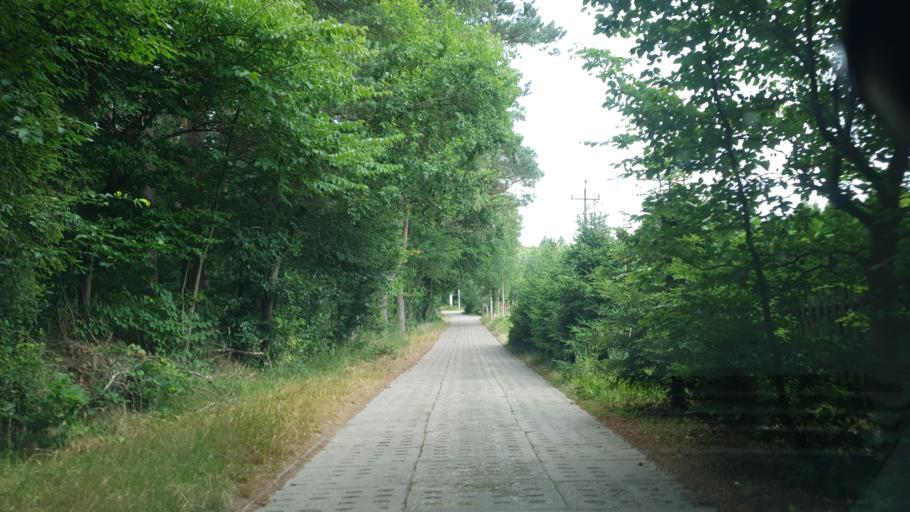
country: PL
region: Pomeranian Voivodeship
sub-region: Powiat kartuski
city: Stezyca
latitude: 54.2477
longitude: 17.9992
